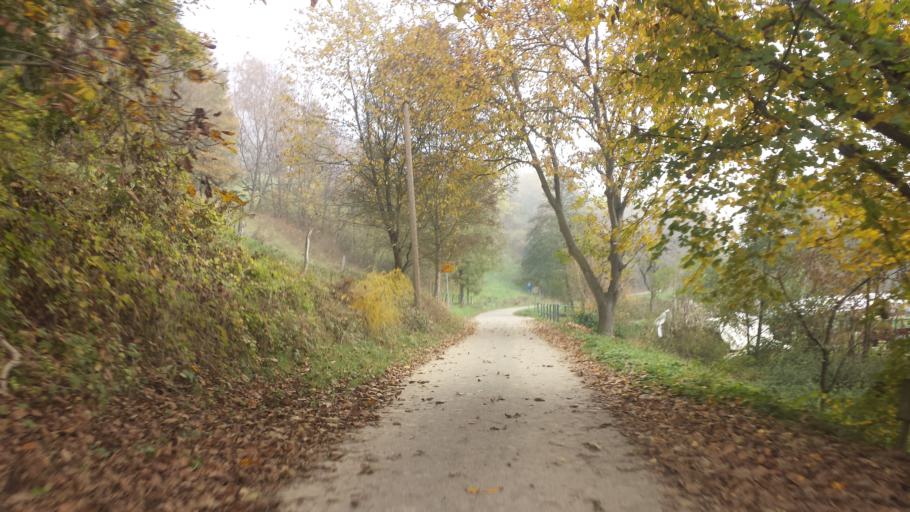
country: DE
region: Hesse
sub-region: Regierungsbezirk Darmstadt
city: Bensheim
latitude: 49.6886
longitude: 8.6813
